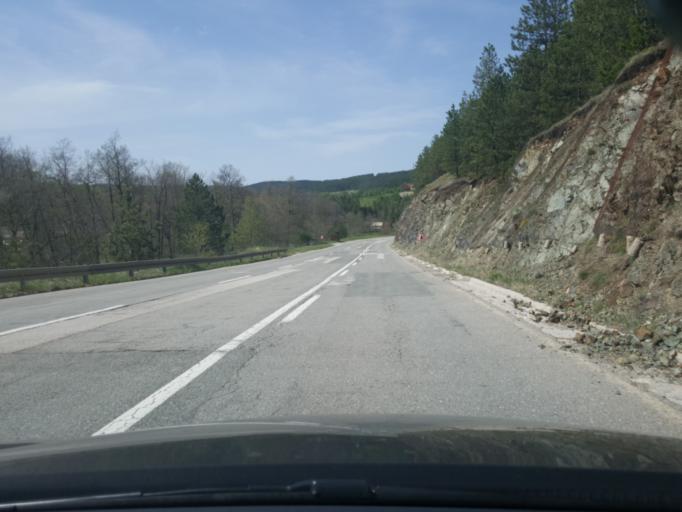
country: RS
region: Central Serbia
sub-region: Zlatiborski Okrug
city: Cajetina
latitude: 43.8368
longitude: 19.6060
